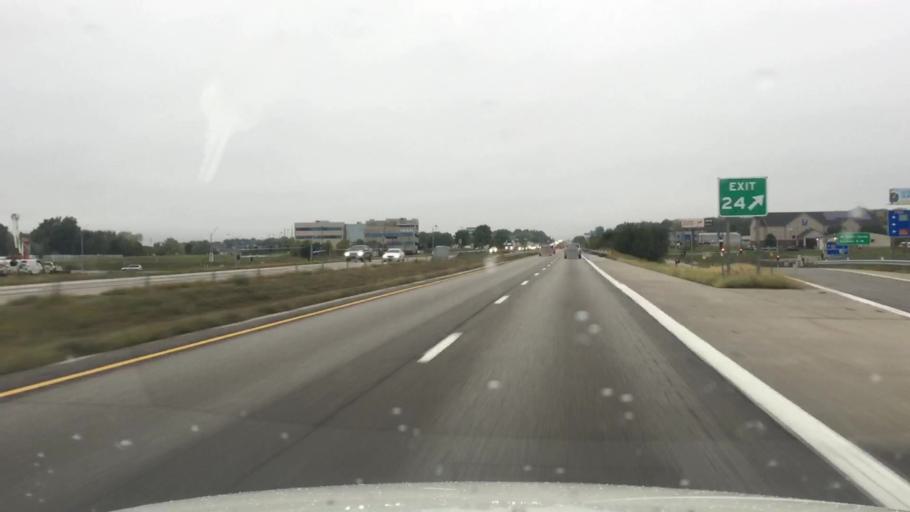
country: US
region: Missouri
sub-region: Jackson County
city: Grain Valley
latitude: 39.0213
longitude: -94.1802
